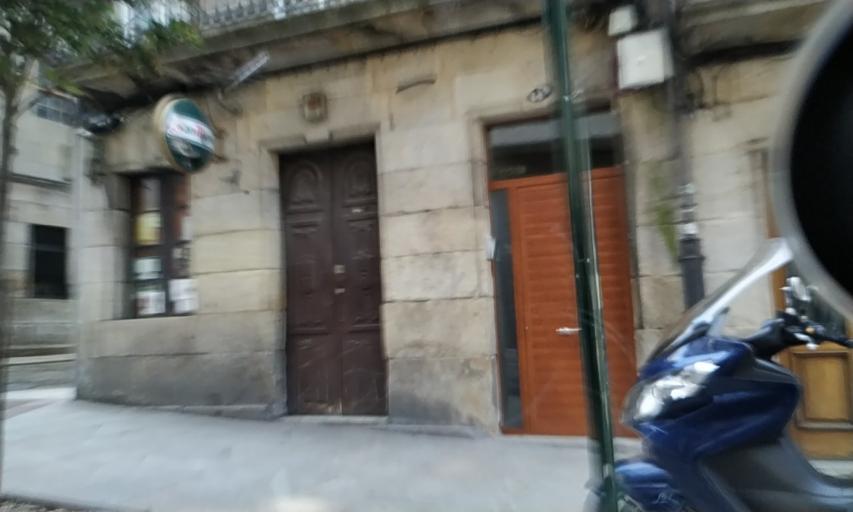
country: ES
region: Galicia
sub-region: Provincia de Pontevedra
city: Vigo
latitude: 42.2342
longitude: -8.7179
